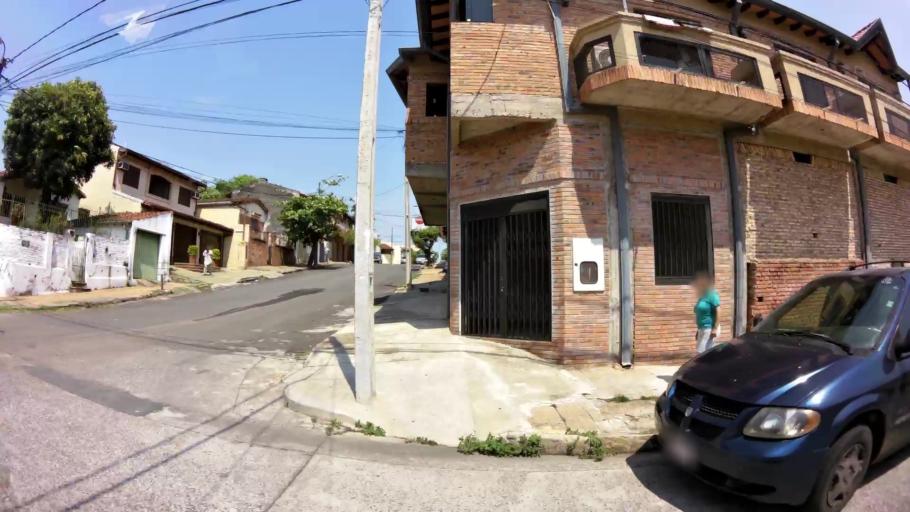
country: PY
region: Presidente Hayes
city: Nanawa
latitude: -25.2780
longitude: -57.6545
